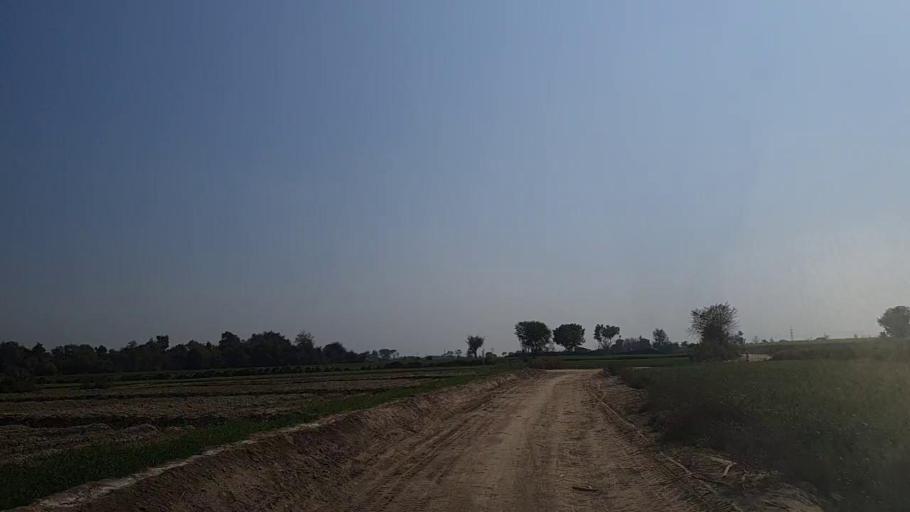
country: PK
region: Sindh
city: Moro
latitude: 26.6982
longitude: 67.9274
